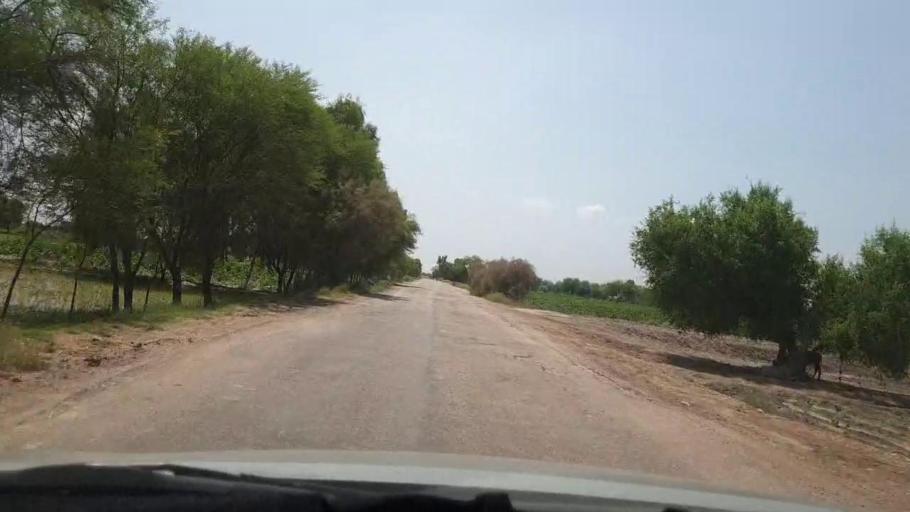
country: PK
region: Sindh
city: Rohri
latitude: 27.6695
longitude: 69.0589
